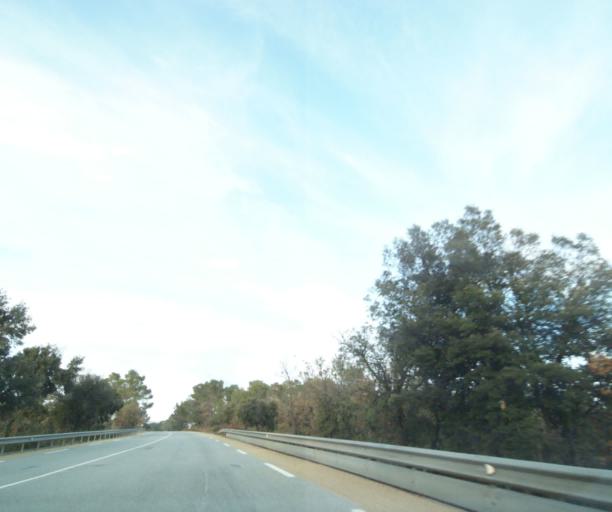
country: FR
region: Provence-Alpes-Cote d'Azur
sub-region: Departement du Var
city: La Motte
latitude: 43.5103
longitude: 6.5165
